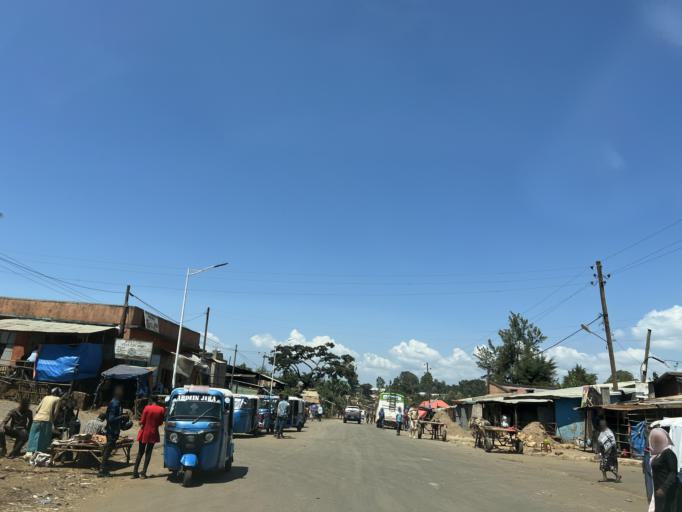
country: ET
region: Oromiya
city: Bedele
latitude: 9.0995
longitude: 36.5393
